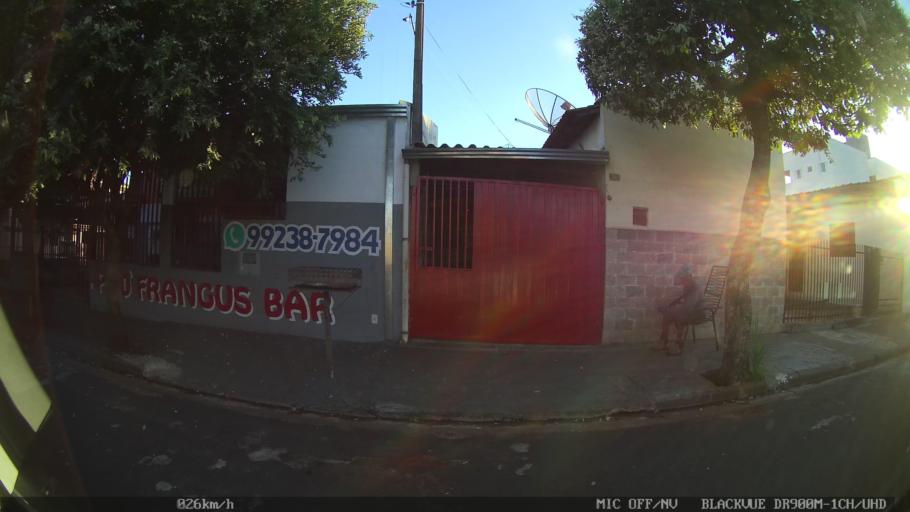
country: BR
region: Sao Paulo
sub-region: Sao Jose Do Rio Preto
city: Sao Jose do Rio Preto
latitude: -20.7995
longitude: -49.3824
